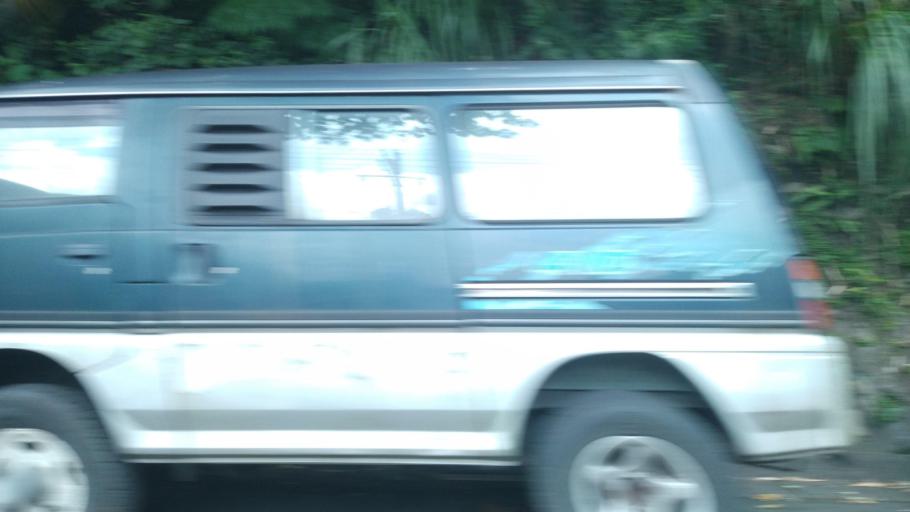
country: TW
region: Taipei
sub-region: Taipei
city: Banqiao
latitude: 24.9505
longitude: 121.4836
